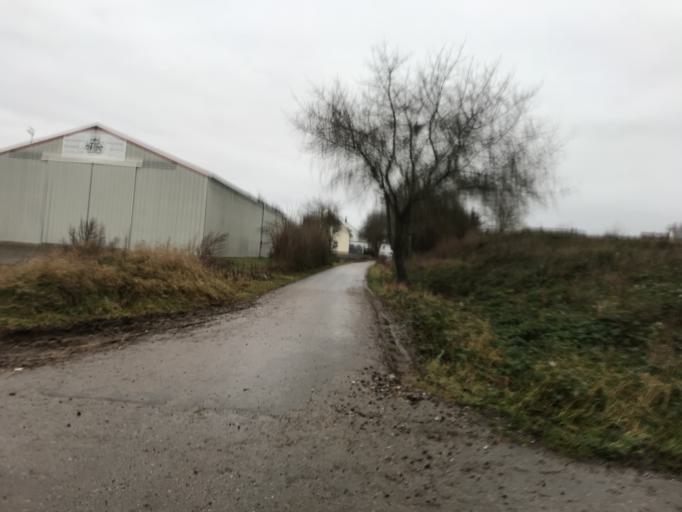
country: DE
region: Rheinland-Pfalz
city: Harxheim
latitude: 49.9012
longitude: 8.2776
